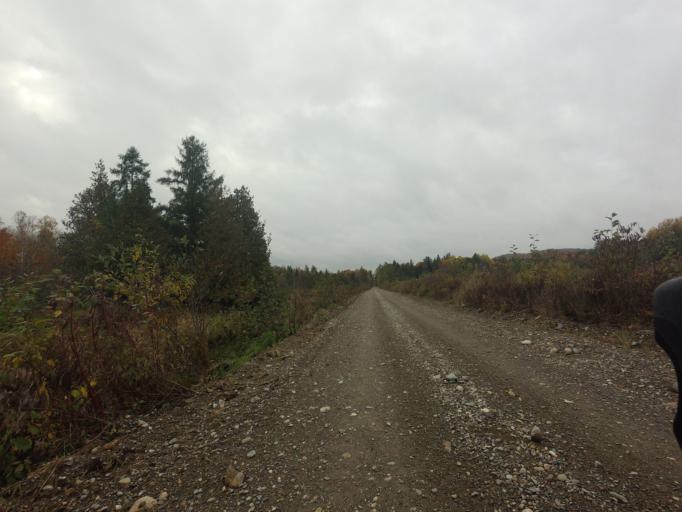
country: CA
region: Ontario
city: Renfrew
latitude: 45.1622
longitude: -76.6844
